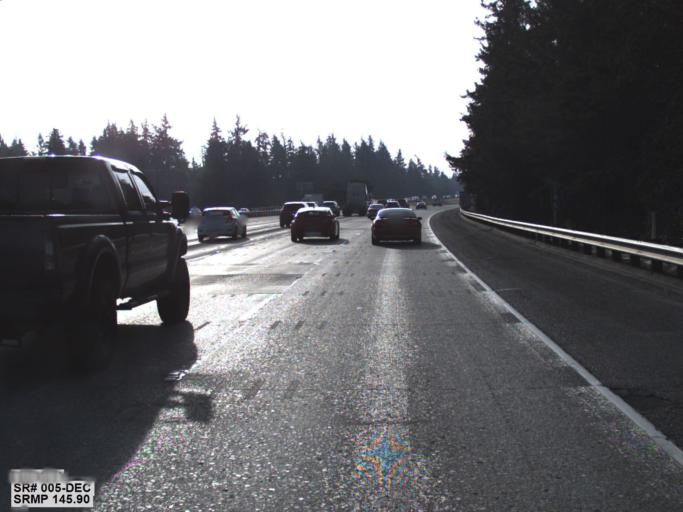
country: US
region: Washington
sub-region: King County
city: Lakeland North
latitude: 47.3447
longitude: -122.2930
